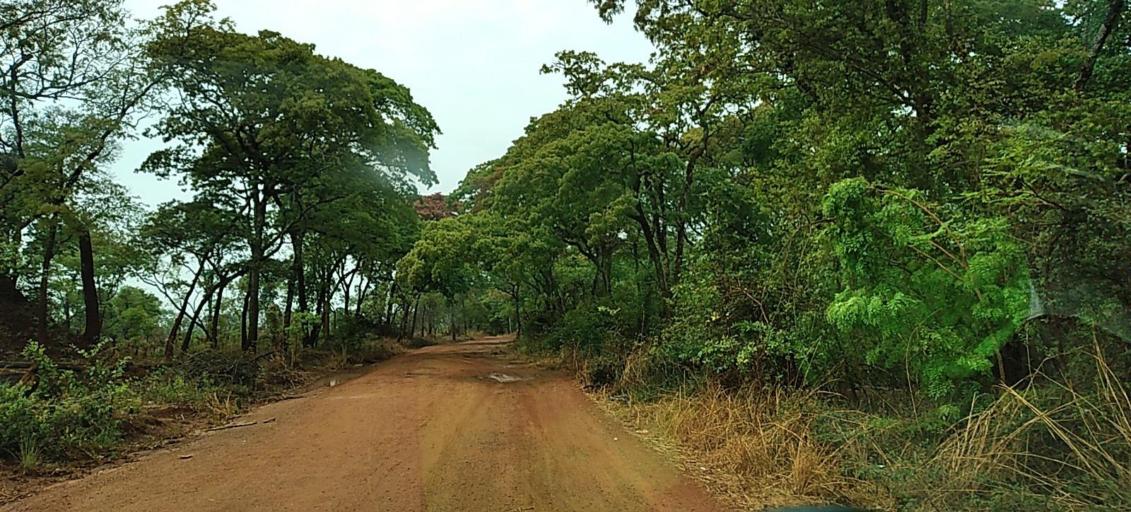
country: ZM
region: North-Western
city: Solwezi
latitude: -12.3124
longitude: 26.5222
